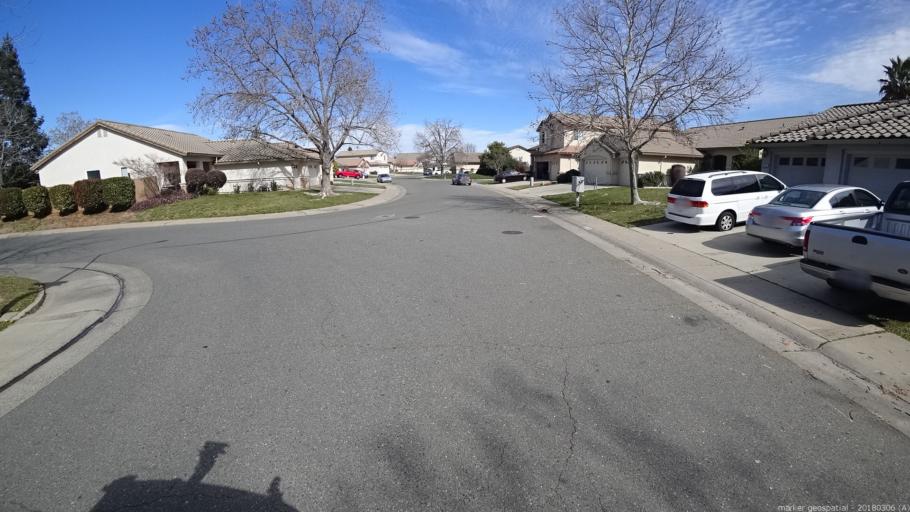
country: US
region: California
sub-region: Sacramento County
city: Vineyard
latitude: 38.4615
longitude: -121.3471
